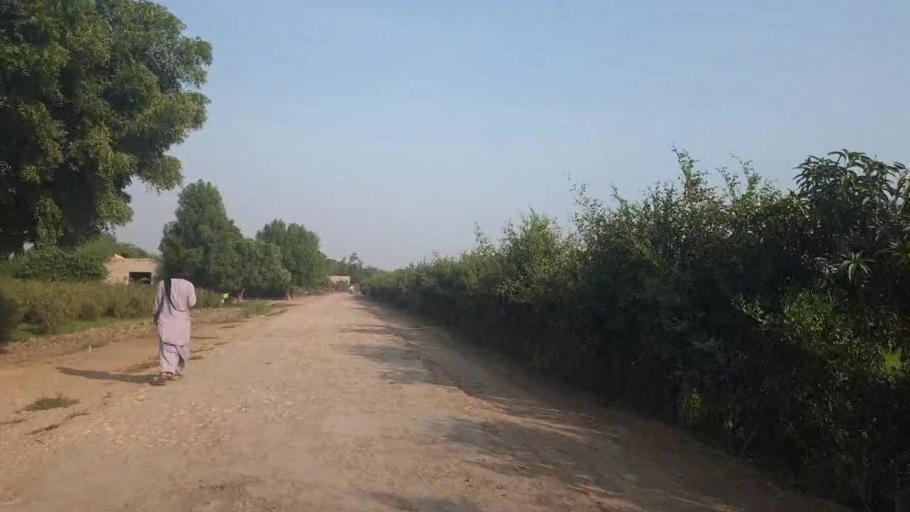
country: PK
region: Sindh
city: Tando Jam
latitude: 25.4252
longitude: 68.4624
